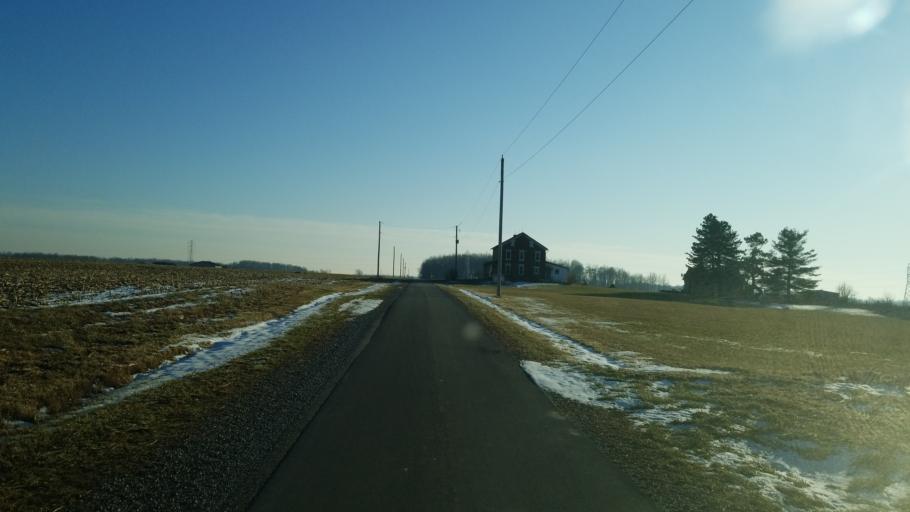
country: US
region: Ohio
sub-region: Crawford County
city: Bucyrus
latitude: 40.9608
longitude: -82.9205
